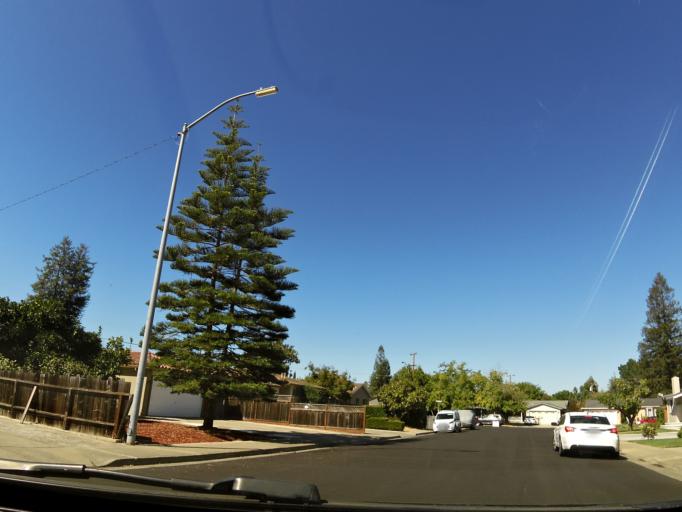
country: US
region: California
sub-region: Santa Clara County
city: Campbell
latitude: 37.2810
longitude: -121.9603
